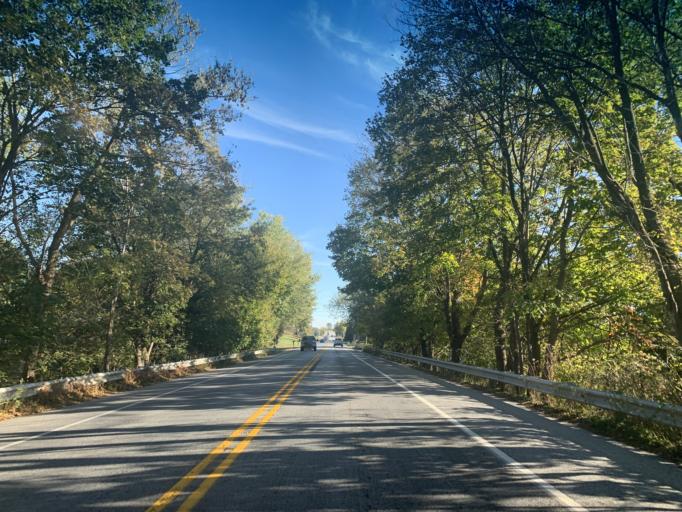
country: US
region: Pennsylvania
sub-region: Chester County
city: Oxford
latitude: 39.8396
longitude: -75.9424
